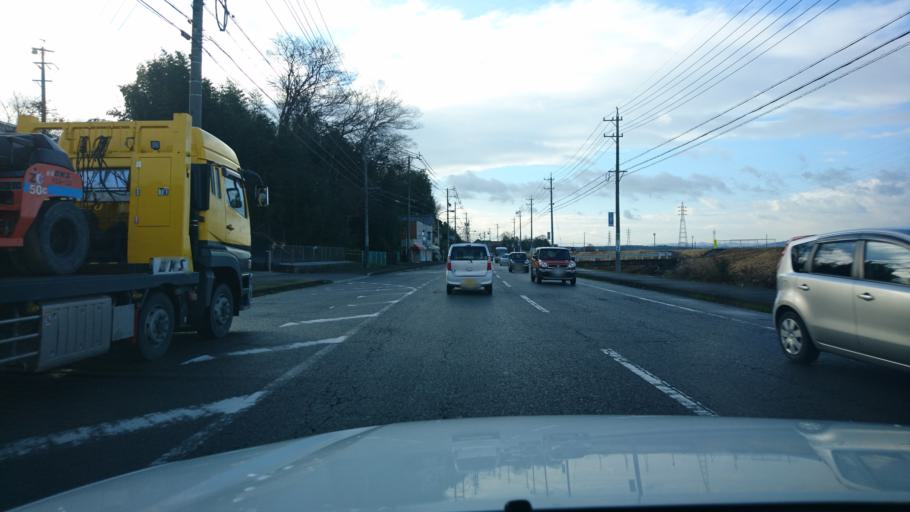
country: JP
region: Mie
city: Ueno-ebisumachi
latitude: 34.7622
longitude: 136.1237
